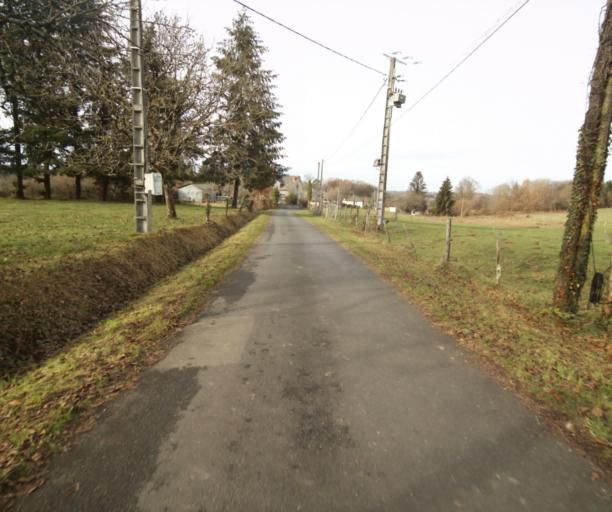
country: FR
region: Limousin
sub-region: Departement de la Correze
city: Saint-Mexant
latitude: 45.2798
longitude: 1.6793
